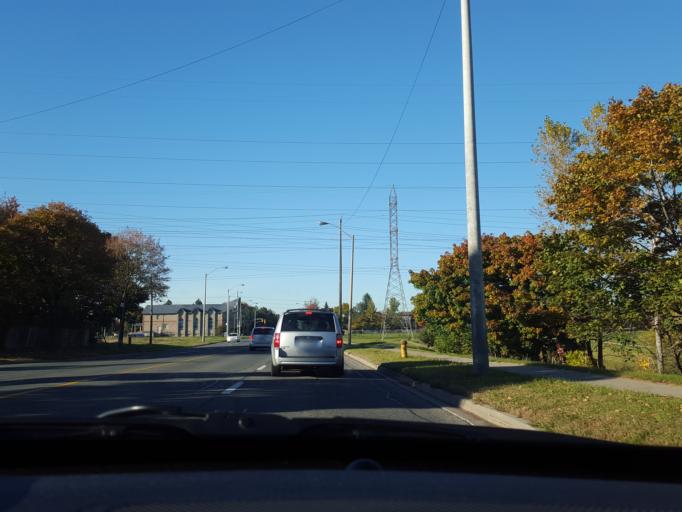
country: CA
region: Ontario
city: Scarborough
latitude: 43.8134
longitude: -79.2807
